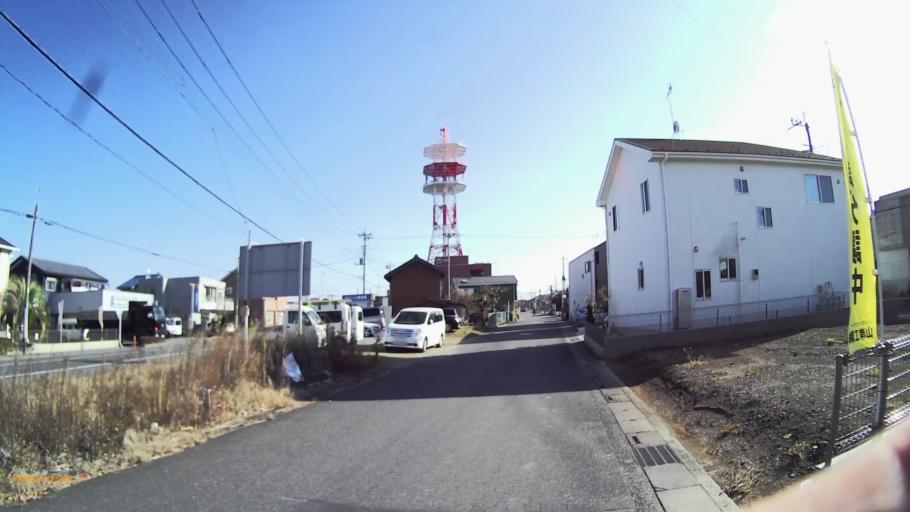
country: JP
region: Saitama
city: Fukiage-fujimi
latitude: 36.1020
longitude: 139.4576
